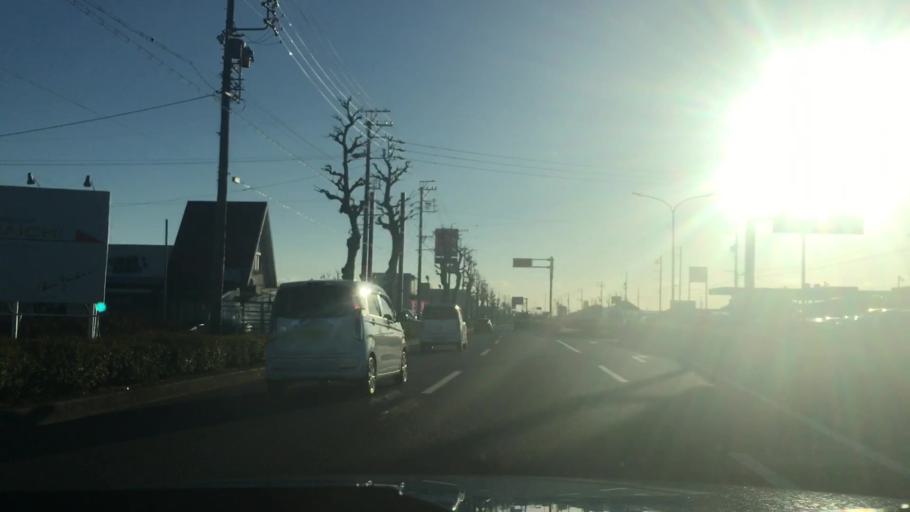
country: JP
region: Shizuoka
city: Hamamatsu
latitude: 34.7601
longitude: 137.6809
